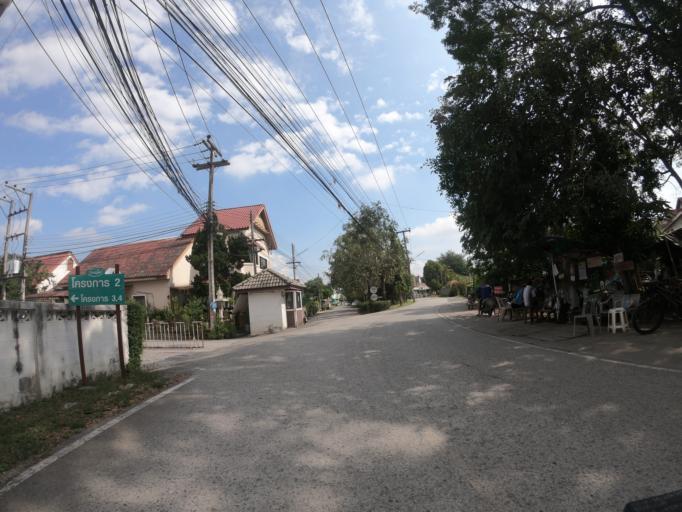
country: TH
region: Chiang Mai
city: Chiang Mai
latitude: 18.7353
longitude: 98.9582
